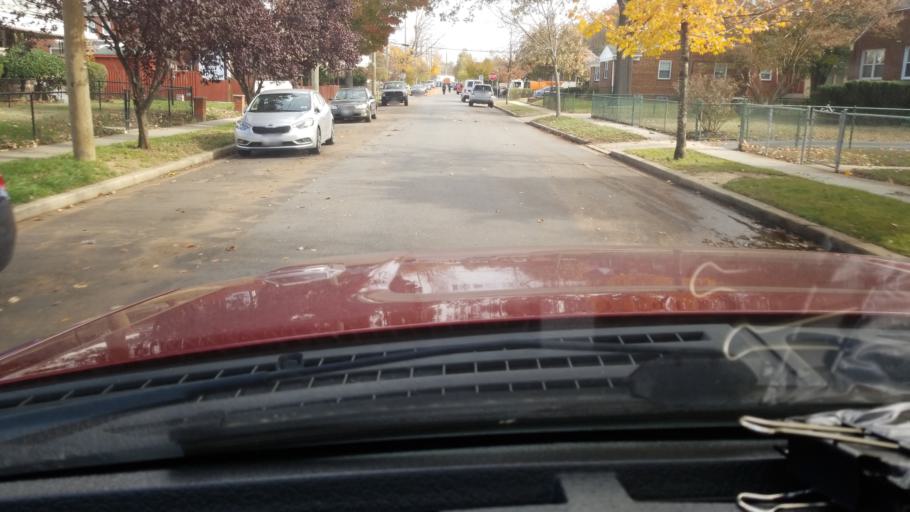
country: US
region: Maryland
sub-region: Prince George's County
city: Colmar Manor
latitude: 38.9056
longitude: -76.9444
